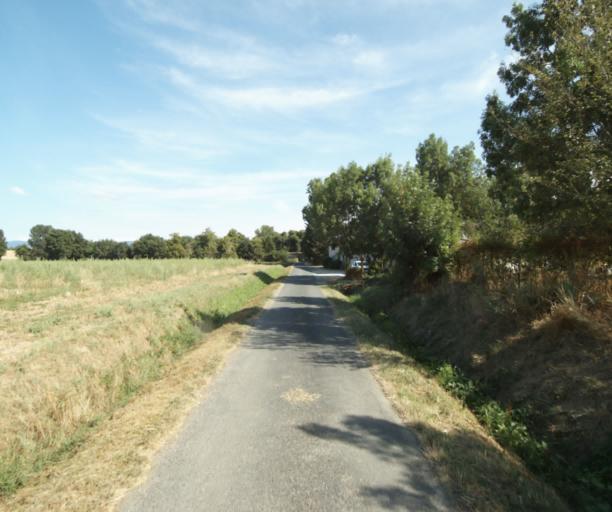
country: FR
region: Midi-Pyrenees
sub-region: Departement de la Haute-Garonne
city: Revel
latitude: 43.5078
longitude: 1.9843
